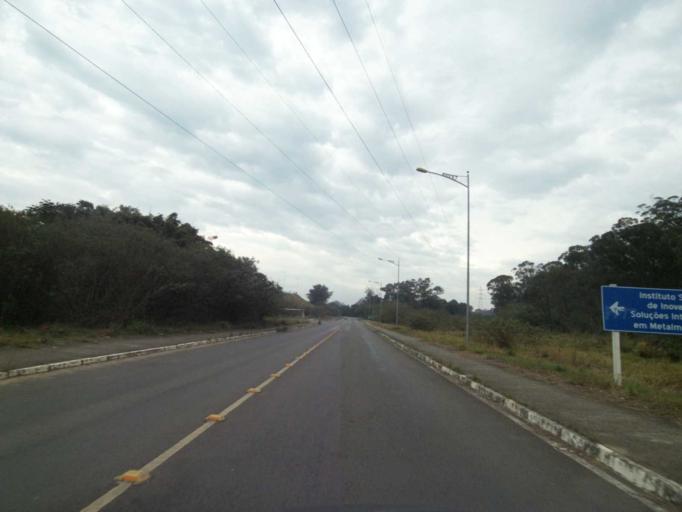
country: BR
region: Rio Grande do Sul
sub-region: Sao Leopoldo
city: Sao Leopoldo
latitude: -29.7859
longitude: -51.1651
